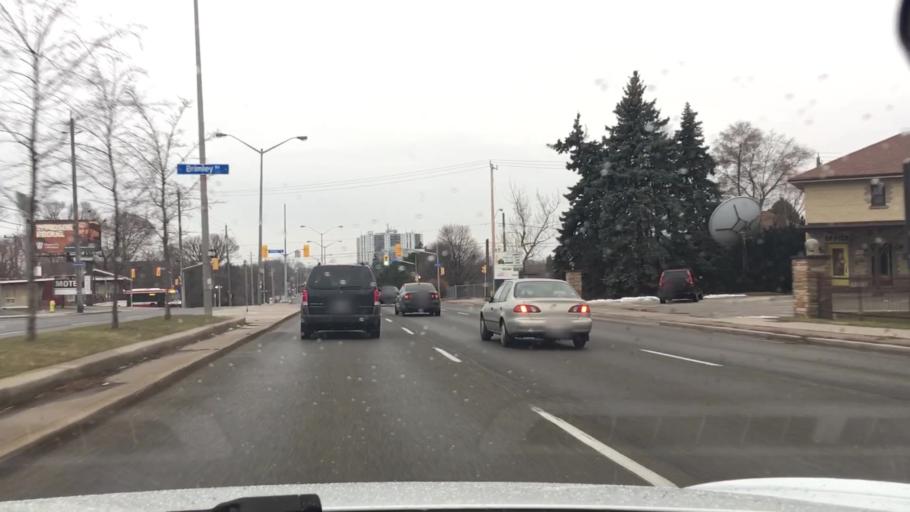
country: CA
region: Ontario
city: Scarborough
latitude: 43.7191
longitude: -79.2395
